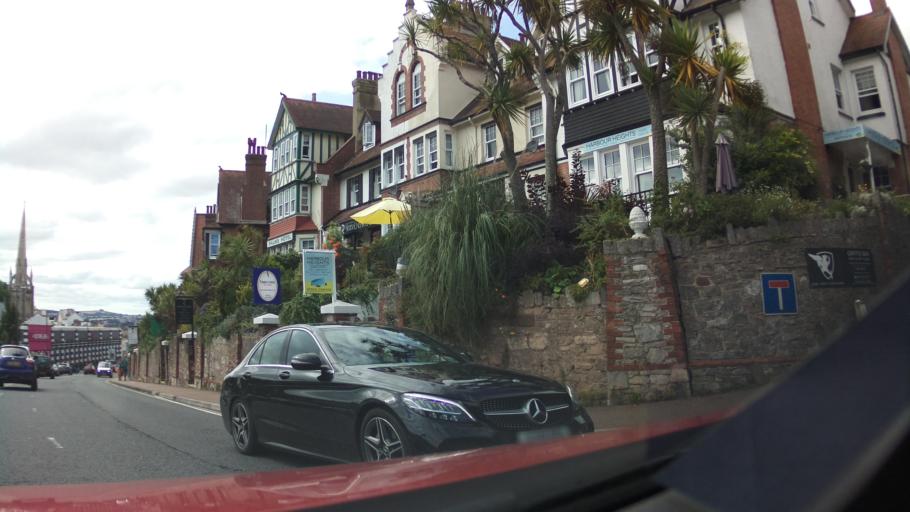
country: GB
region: England
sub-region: Borough of Torbay
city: Torquay
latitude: 50.4624
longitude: -3.5183
